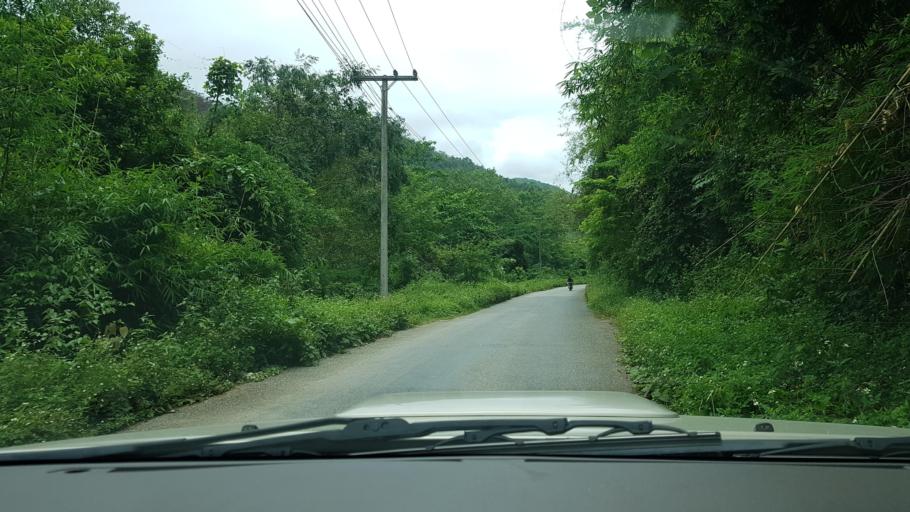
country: LA
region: Phongsali
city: Khoa
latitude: 21.0497
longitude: 102.4088
